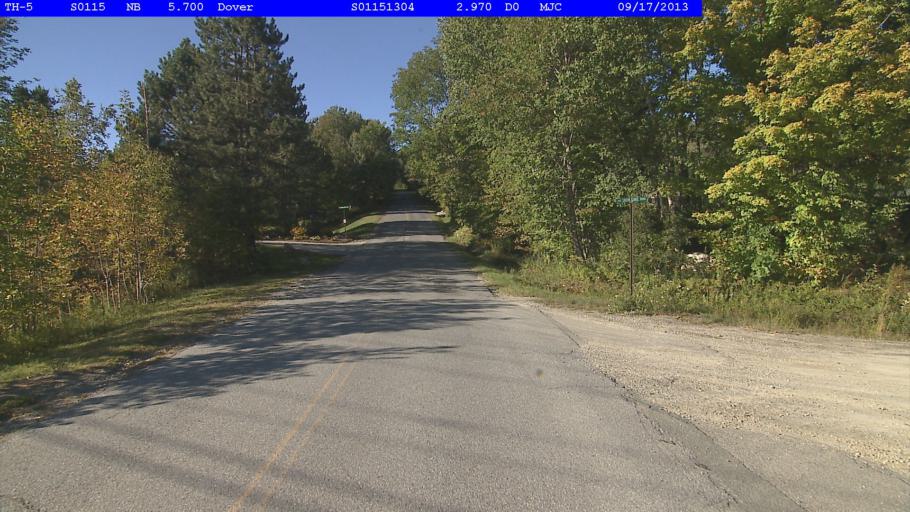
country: US
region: Vermont
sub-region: Windham County
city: Dover
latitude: 42.9669
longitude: -72.8896
